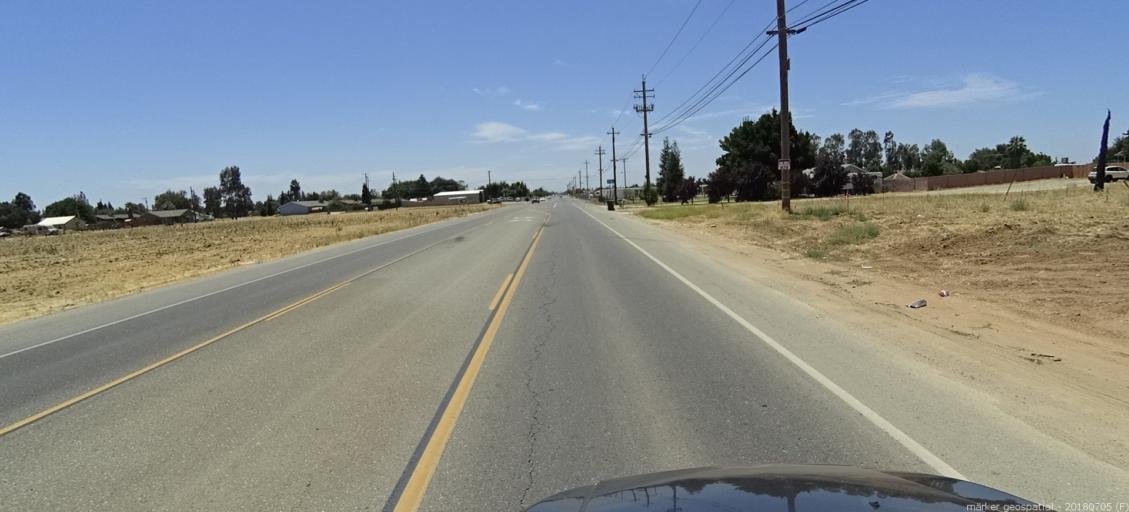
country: US
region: California
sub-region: Madera County
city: Madera Acres
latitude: 37.0051
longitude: -120.0743
